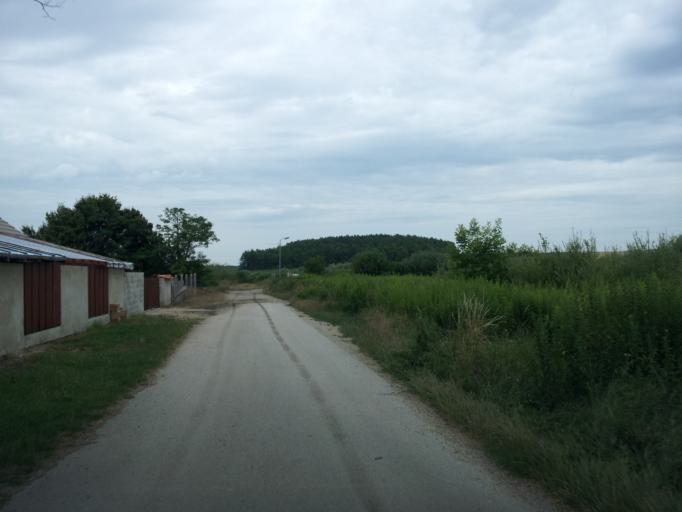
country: HU
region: Veszprem
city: Devecser
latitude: 47.0956
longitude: 17.4459
